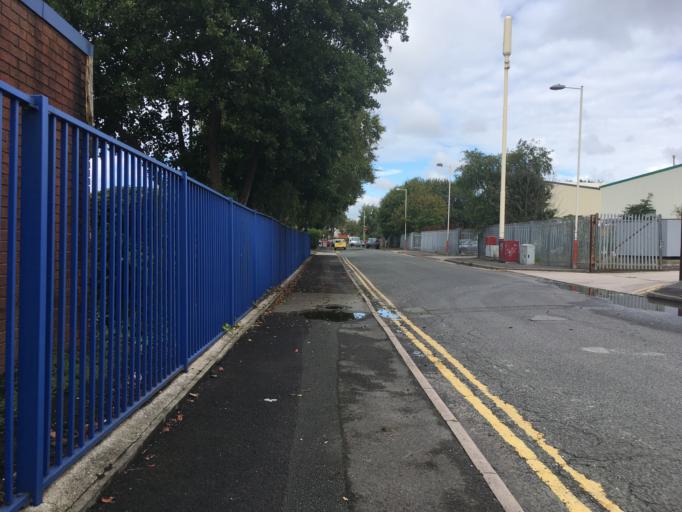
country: GB
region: England
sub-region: Sefton
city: Southport
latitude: 53.6416
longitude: -2.9693
